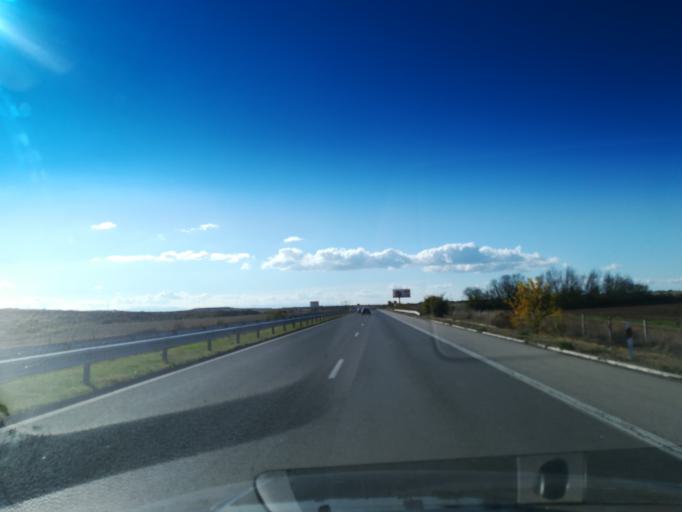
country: BG
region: Stara Zagora
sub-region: Obshtina Chirpan
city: Chirpan
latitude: 42.2470
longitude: 25.3982
